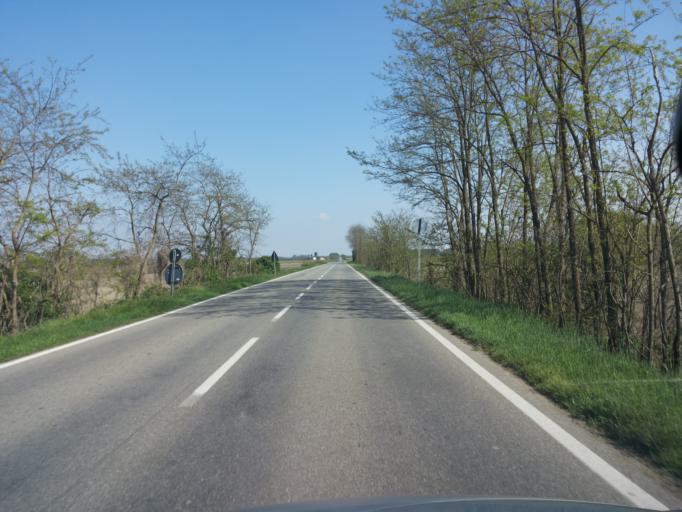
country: IT
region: Piedmont
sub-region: Provincia di Vercelli
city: Caresana
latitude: 45.2147
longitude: 8.5092
